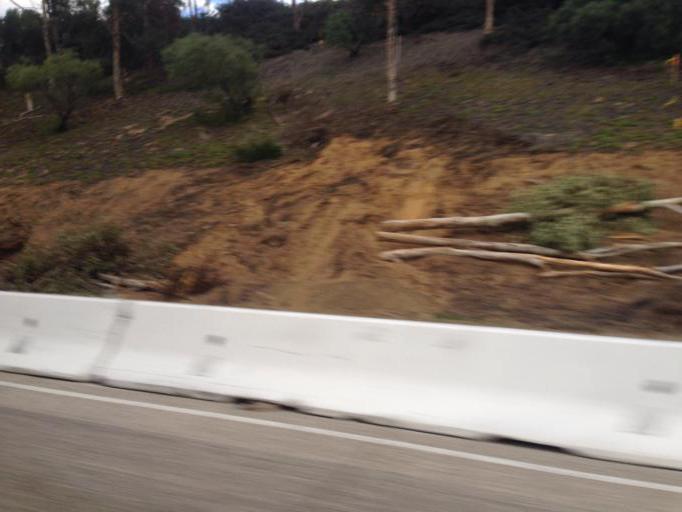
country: US
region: California
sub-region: San Diego County
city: National City
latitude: 32.6672
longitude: -117.0802
